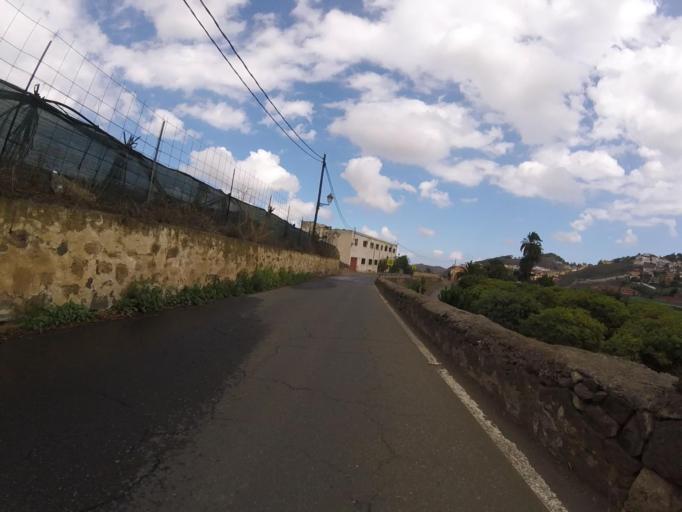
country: ES
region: Canary Islands
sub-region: Provincia de Las Palmas
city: Santa Brigida
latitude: 28.0456
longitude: -15.4849
